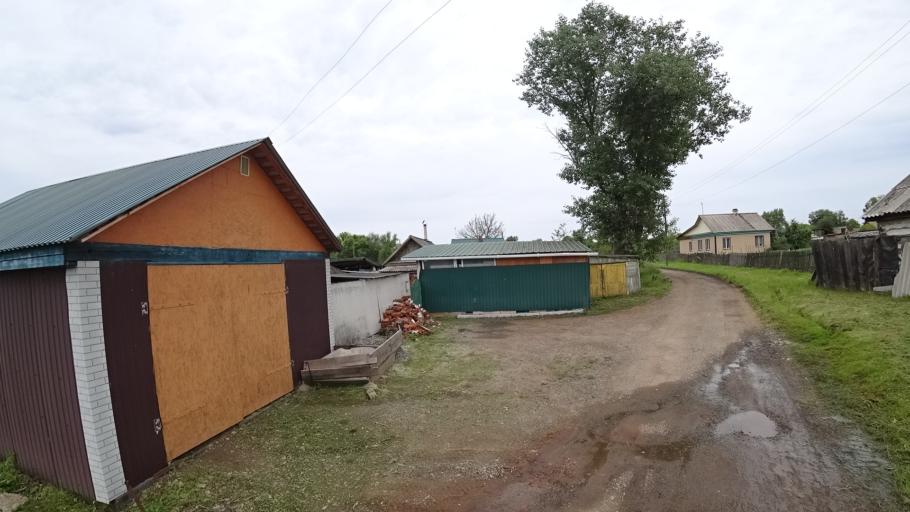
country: RU
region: Primorskiy
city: Novosysoyevka
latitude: 44.2085
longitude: 133.3382
